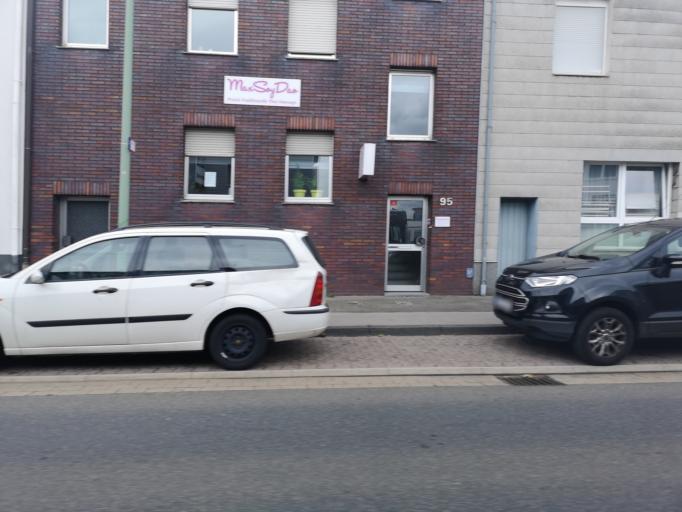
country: DE
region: North Rhine-Westphalia
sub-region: Regierungsbezirk Koln
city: Kreuzau
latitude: 50.7717
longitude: 6.4921
